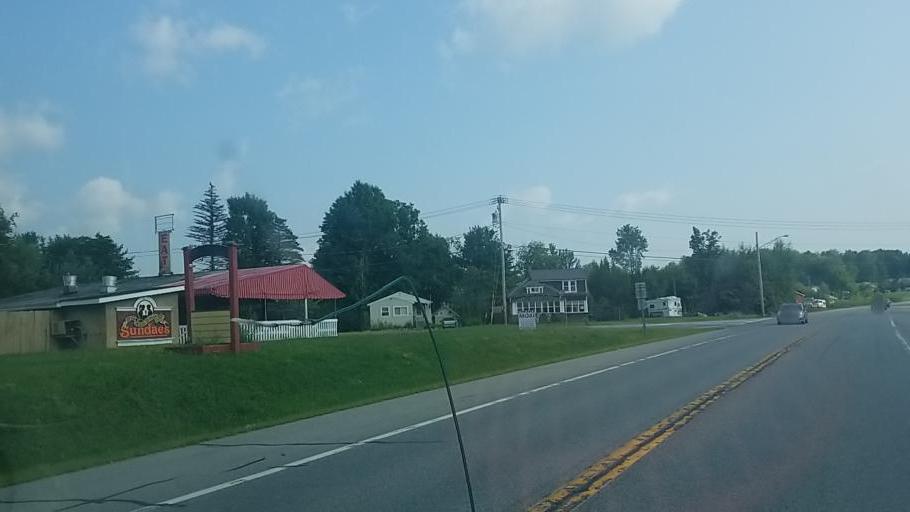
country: US
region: New York
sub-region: Fulton County
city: Gloversville
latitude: 43.1013
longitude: -74.2755
